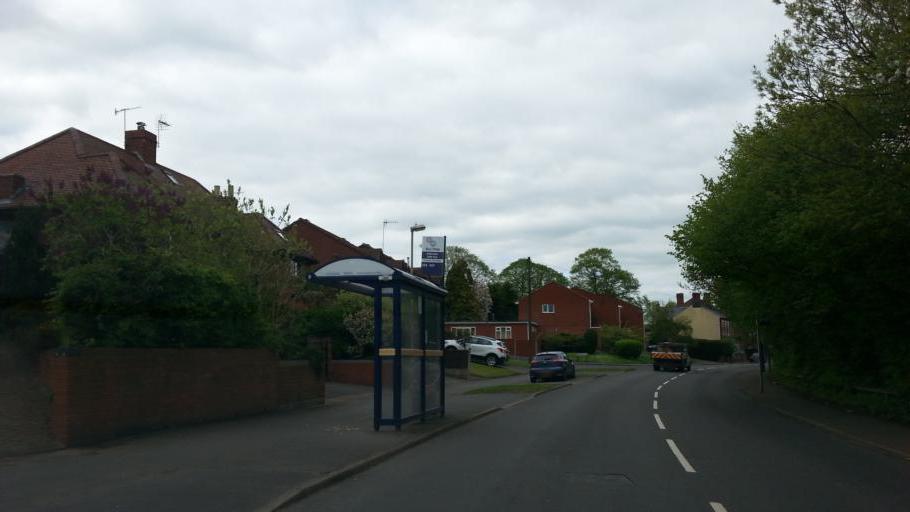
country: GB
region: England
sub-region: Dudley
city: Kingswinford
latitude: 52.4784
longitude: -2.1676
